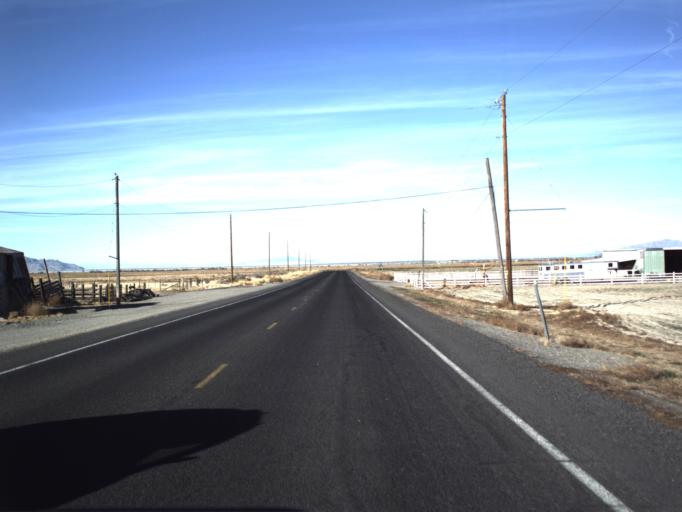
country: US
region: Utah
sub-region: Tooele County
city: Erda
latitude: 40.6088
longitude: -112.3709
